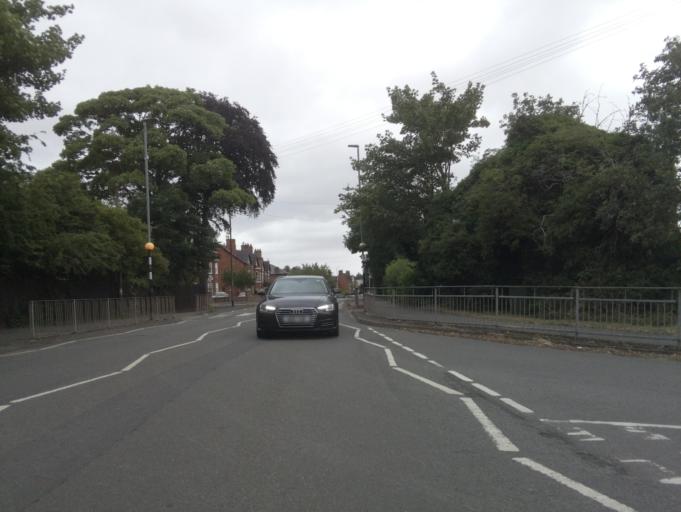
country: GB
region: England
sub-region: Leicestershire
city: Ashby de la Zouch
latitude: 52.7410
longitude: -1.4796
